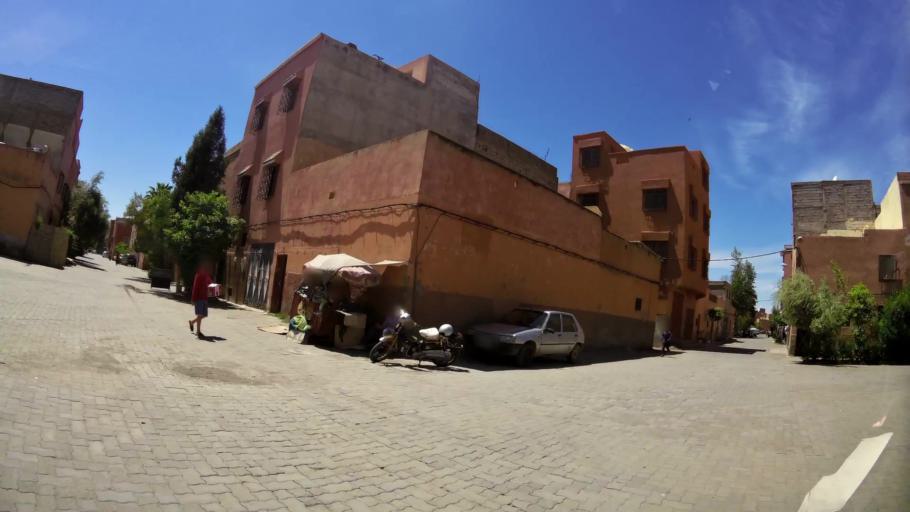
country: MA
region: Marrakech-Tensift-Al Haouz
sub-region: Marrakech
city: Marrakesh
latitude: 31.6301
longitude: -8.0442
